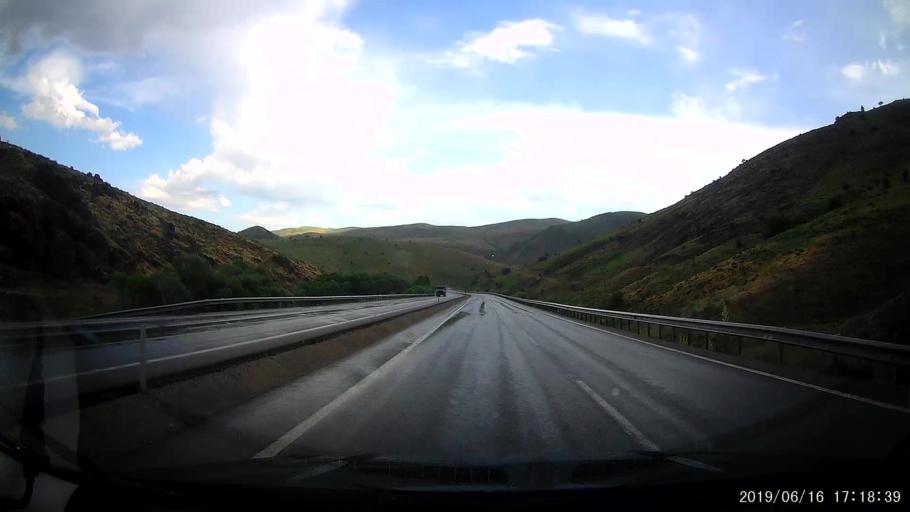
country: TR
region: Erzincan
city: Tercan
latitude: 39.8110
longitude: 40.5290
